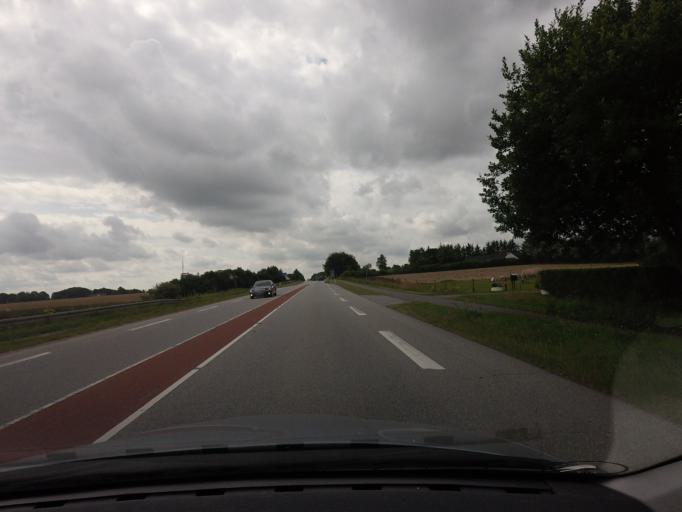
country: DK
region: North Denmark
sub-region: Hjorring Kommune
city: Hjorring
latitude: 57.4045
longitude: 9.9883
